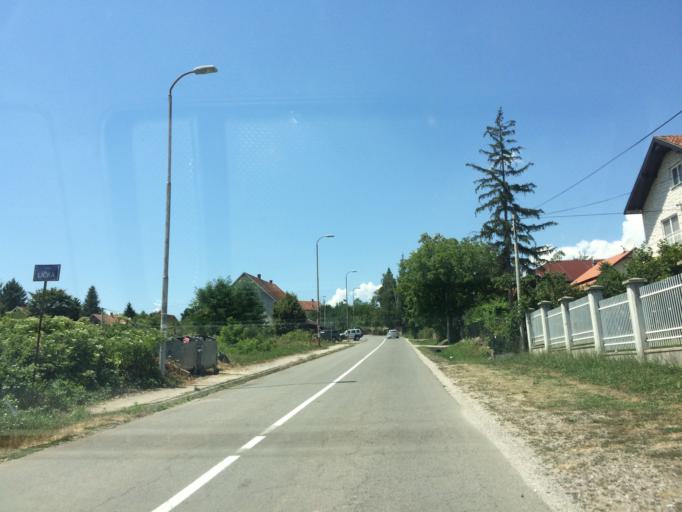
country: RS
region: Central Serbia
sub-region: Kolubarski Okrug
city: Mionica
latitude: 44.2270
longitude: 20.1572
